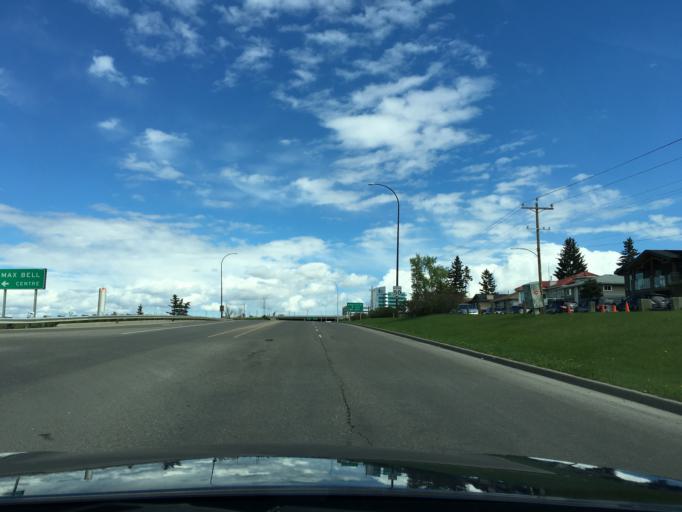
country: CA
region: Alberta
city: Calgary
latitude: 51.0403
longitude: -114.0019
